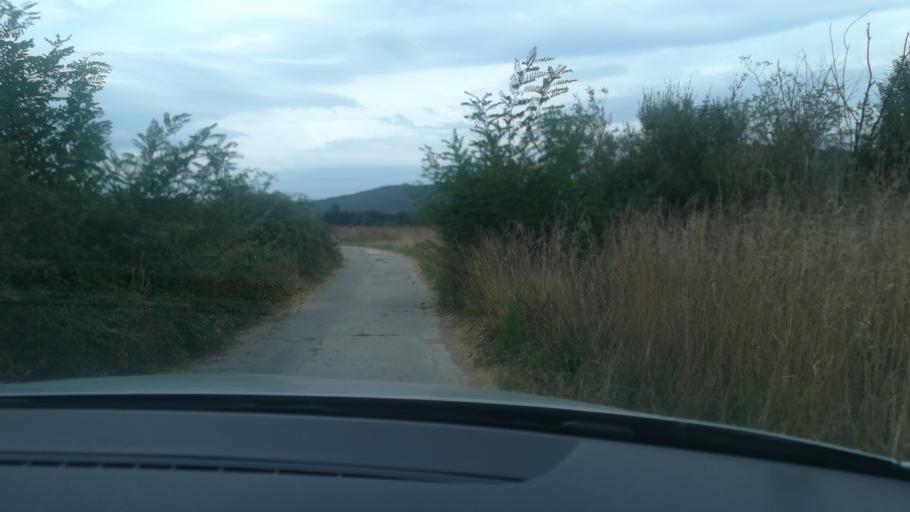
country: MK
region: Debarca
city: Belcista
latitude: 41.2921
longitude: 20.8320
